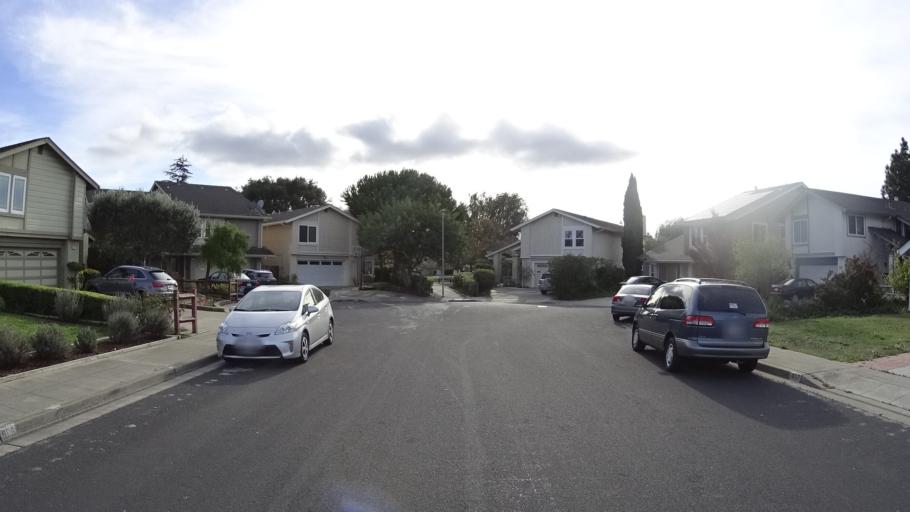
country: US
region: California
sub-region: San Mateo County
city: Foster City
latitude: 37.5472
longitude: -122.2667
